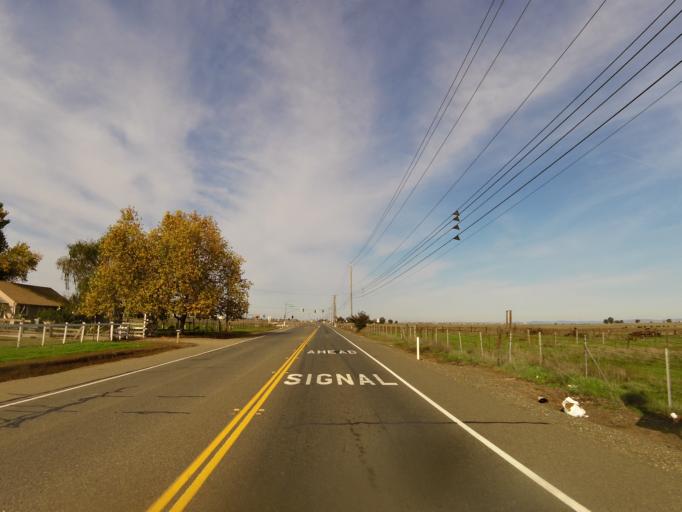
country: US
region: California
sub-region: Sacramento County
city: Wilton
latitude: 38.4947
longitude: -121.2422
